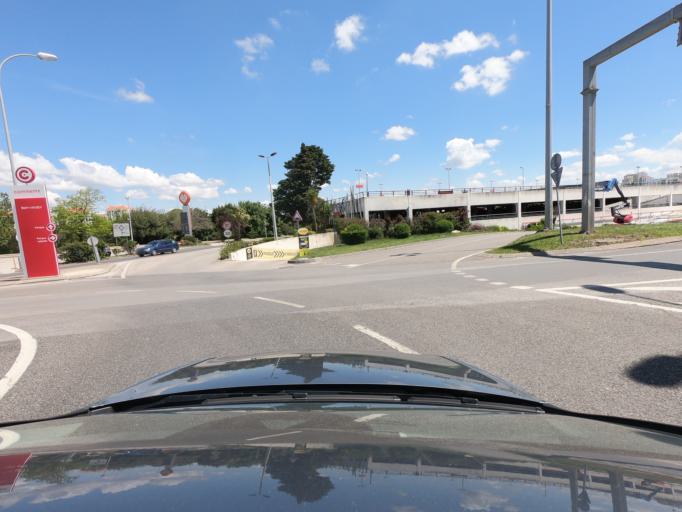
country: PT
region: Lisbon
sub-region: Amadora
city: Amadora
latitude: 38.7432
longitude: -9.2348
